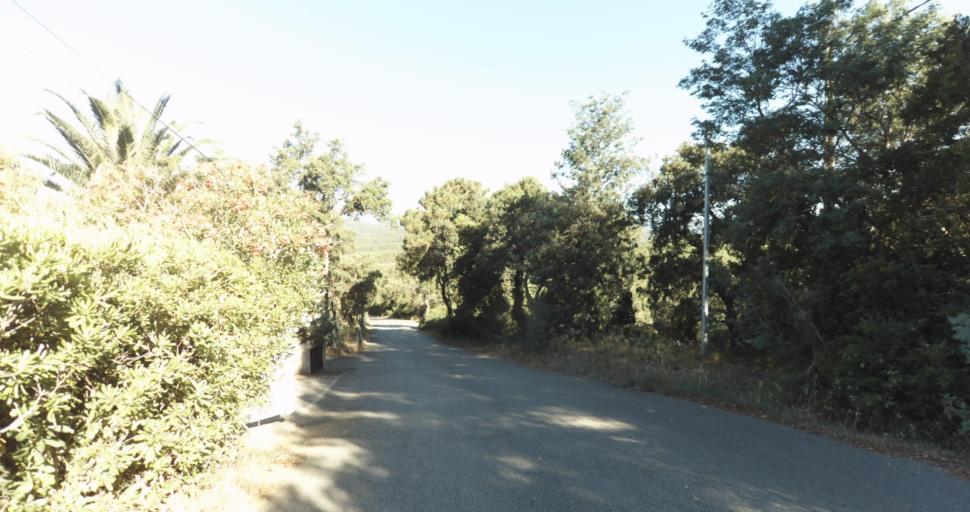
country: FR
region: Provence-Alpes-Cote d'Azur
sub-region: Departement du Var
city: Gassin
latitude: 43.2161
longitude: 6.5853
